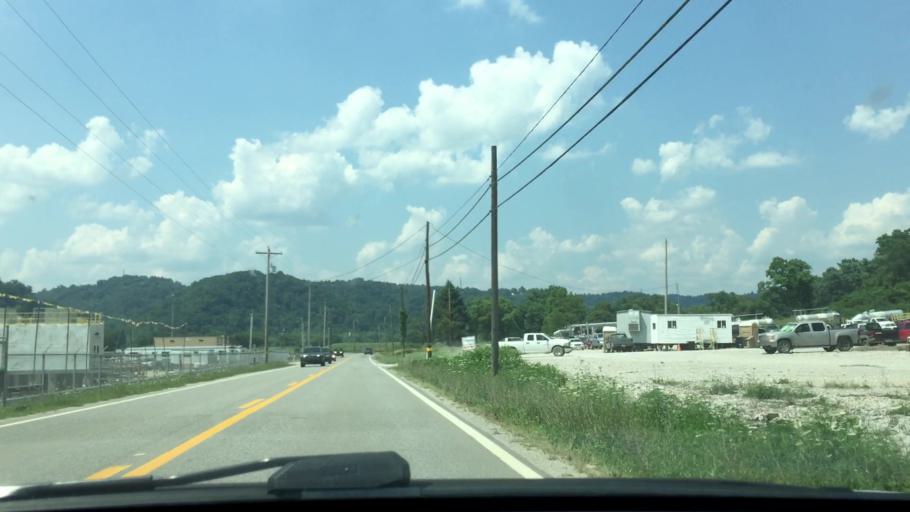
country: US
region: Ohio
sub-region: Belmont County
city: Powhatan Point
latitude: 39.7622
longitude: -80.8605
